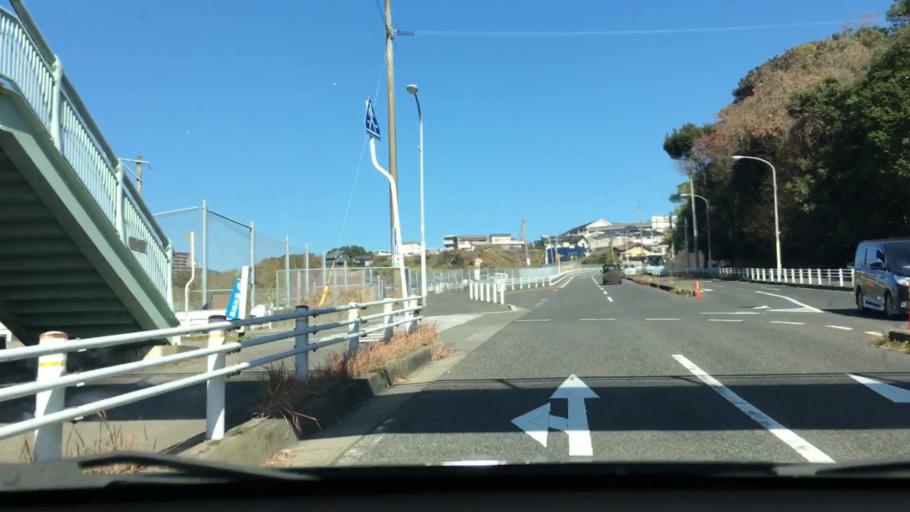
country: JP
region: Kagoshima
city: Kagoshima-shi
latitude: 31.5576
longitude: 130.5261
